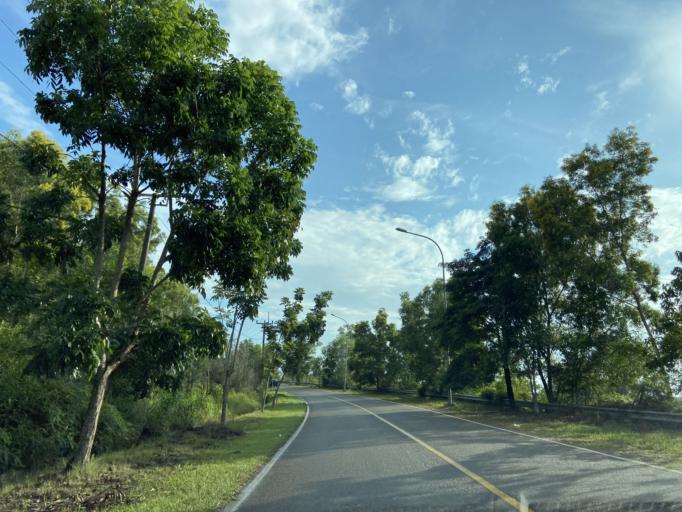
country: SG
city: Singapore
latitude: 0.9641
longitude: 104.0560
